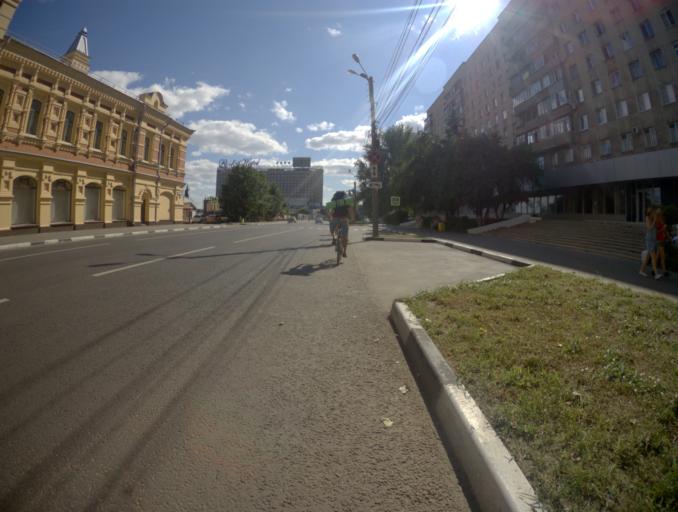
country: RU
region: Nizjnij Novgorod
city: Nizhniy Novgorod
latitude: 56.3281
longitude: 43.9602
